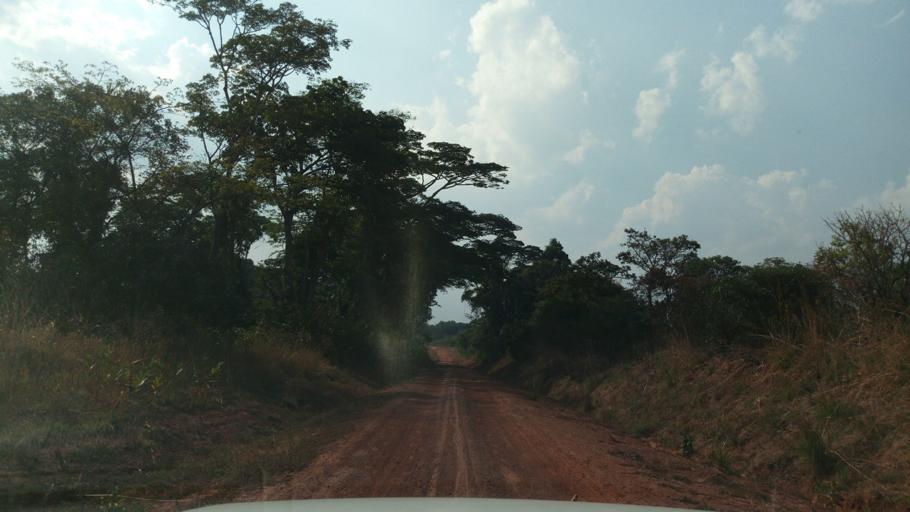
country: CD
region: Katanga
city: Kalemie
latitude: -5.2354
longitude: 28.8740
